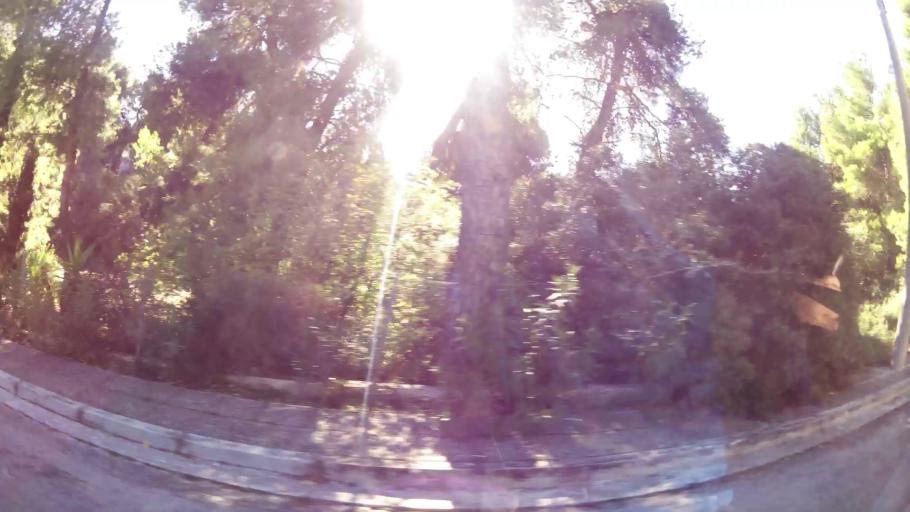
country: GR
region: Attica
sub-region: Nomarchia Athinas
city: Ekali
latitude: 38.1155
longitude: 23.8480
